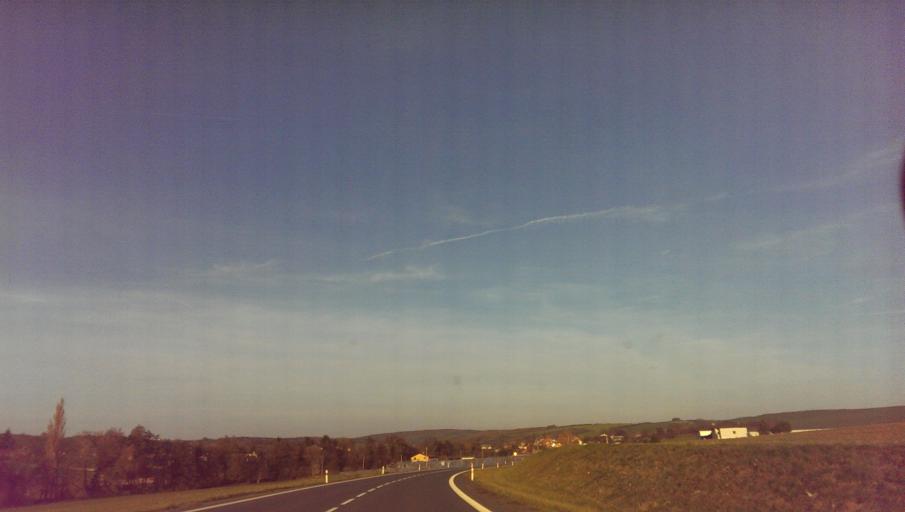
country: CZ
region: Zlin
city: Brezolupy
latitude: 49.1125
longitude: 17.5666
